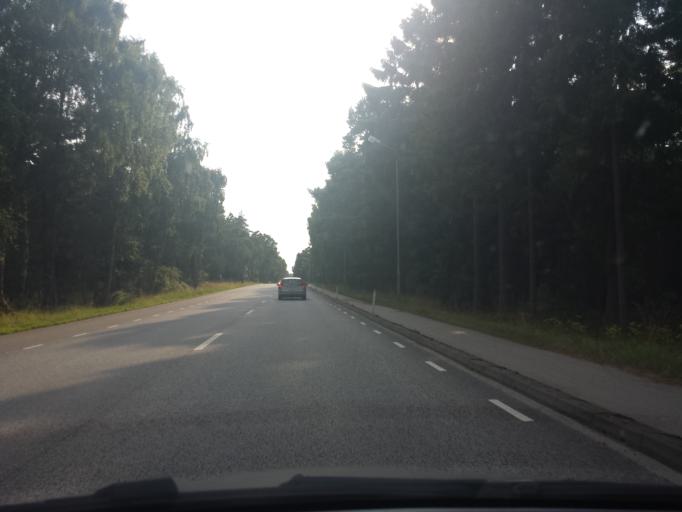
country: SE
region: Skane
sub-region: Ystads Kommun
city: Kopingebro
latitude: 55.4361
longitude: 13.8874
